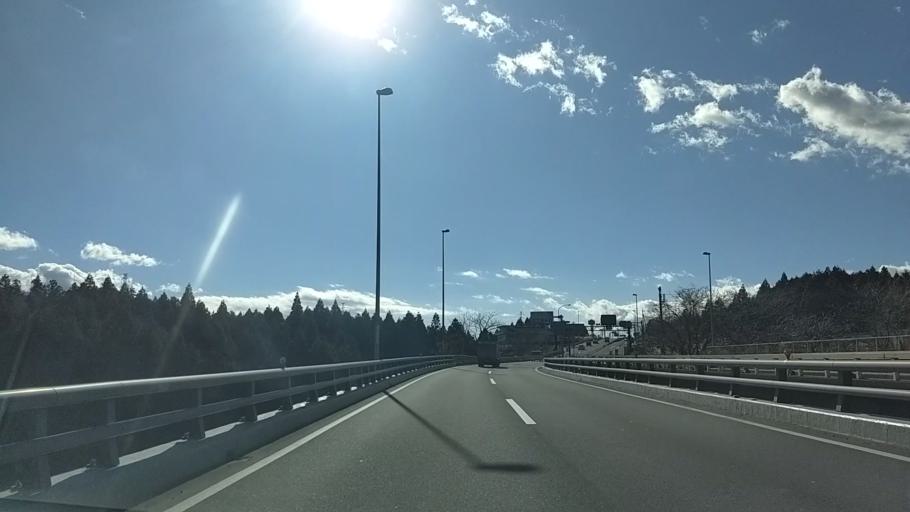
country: JP
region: Shizuoka
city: Gotemba
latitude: 35.3530
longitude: 138.9541
